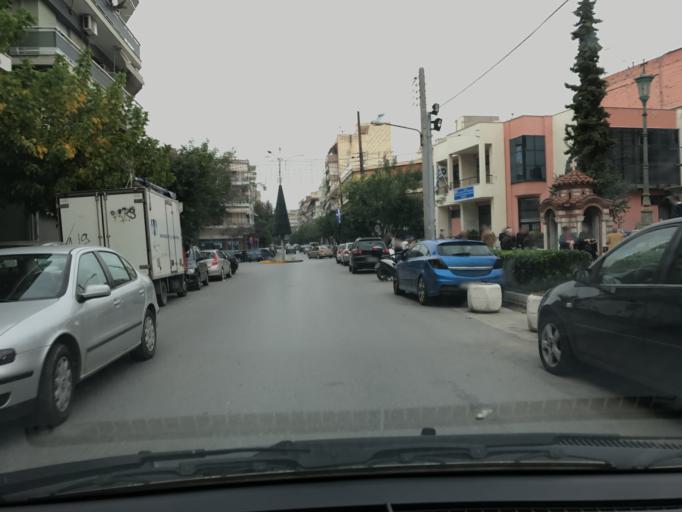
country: GR
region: Central Macedonia
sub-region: Nomos Thessalonikis
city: Ampelokipoi
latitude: 40.6512
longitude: 22.9281
